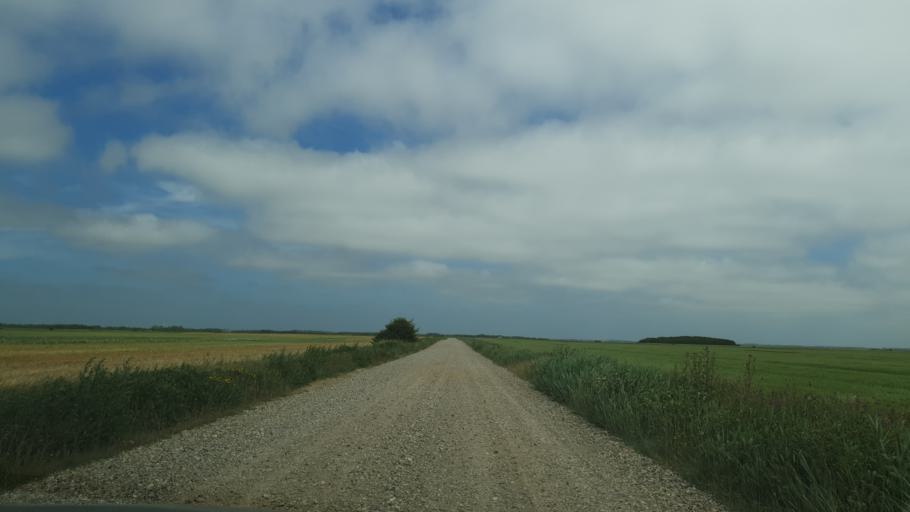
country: DK
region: Central Jutland
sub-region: Ringkobing-Skjern Kommune
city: Skjern
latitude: 55.9354
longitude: 8.4181
